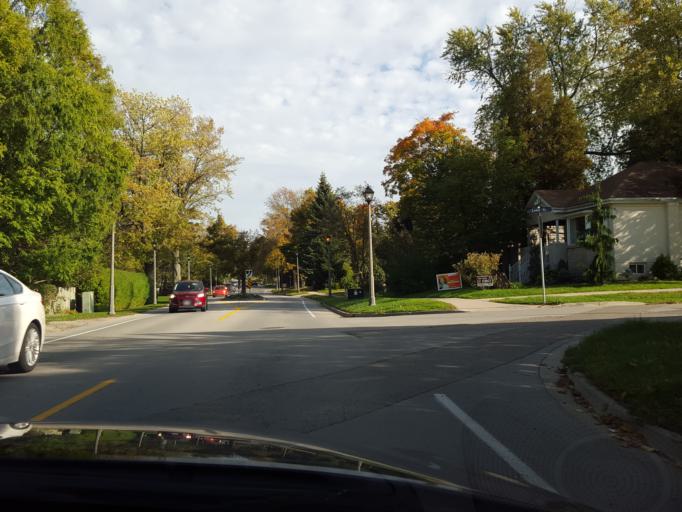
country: CA
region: Ontario
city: Ancaster
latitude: 43.2302
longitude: -79.9726
